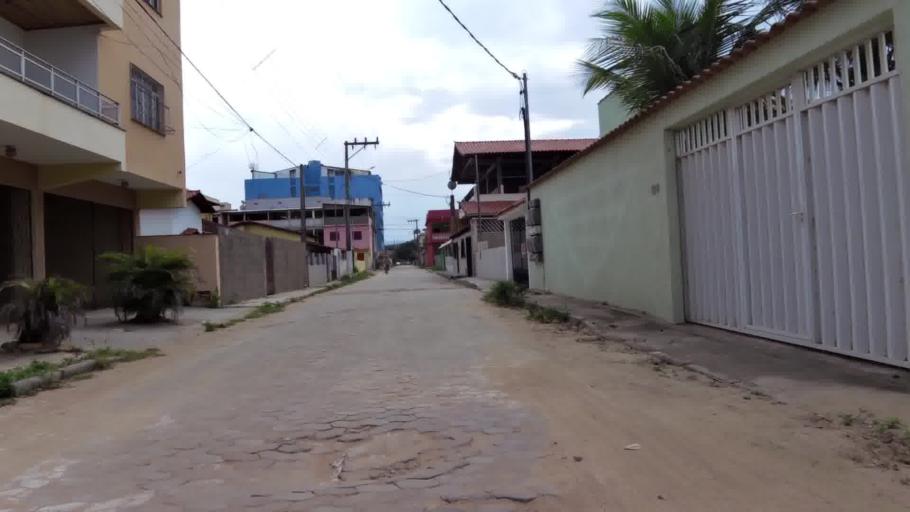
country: BR
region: Espirito Santo
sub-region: Piuma
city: Piuma
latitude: -20.8426
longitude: -40.7337
